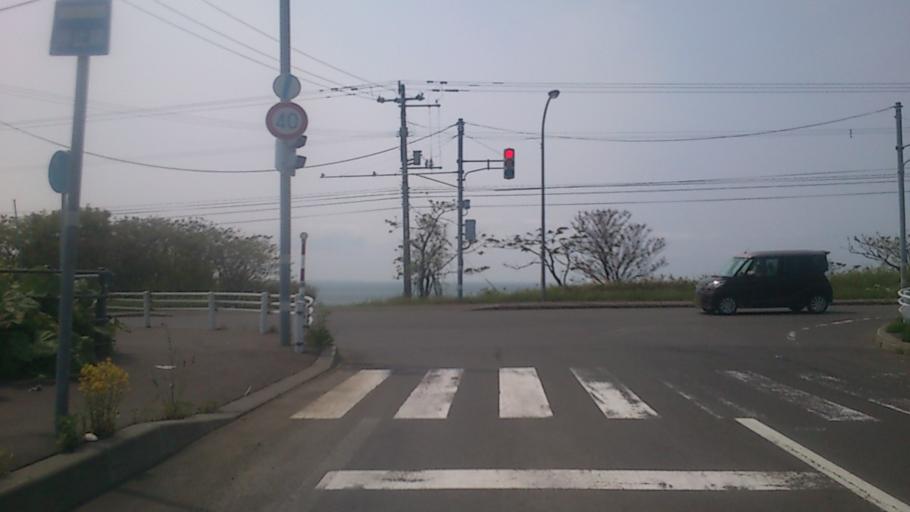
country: JP
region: Hokkaido
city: Nemuro
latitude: 43.2820
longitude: 145.5076
